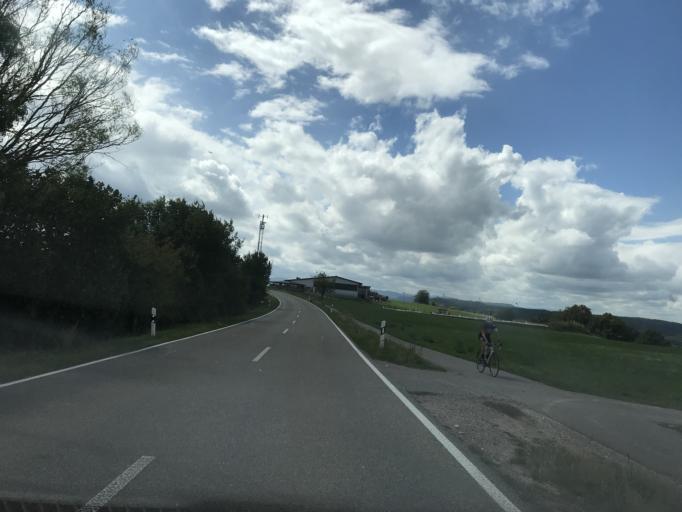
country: DE
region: Baden-Wuerttemberg
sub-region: Freiburg Region
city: Steinen
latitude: 47.6058
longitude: 7.7599
